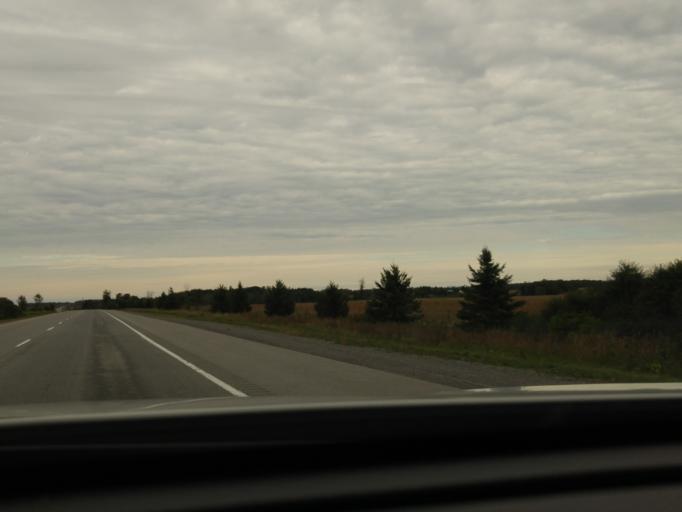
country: CA
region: Ontario
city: Arnprior
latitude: 45.3845
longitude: -76.2623
